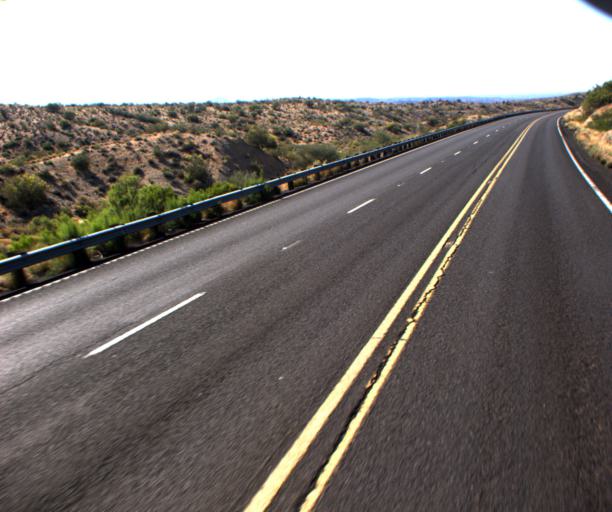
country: US
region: Arizona
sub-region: Mohave County
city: Kingman
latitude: 34.9308
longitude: -113.6597
